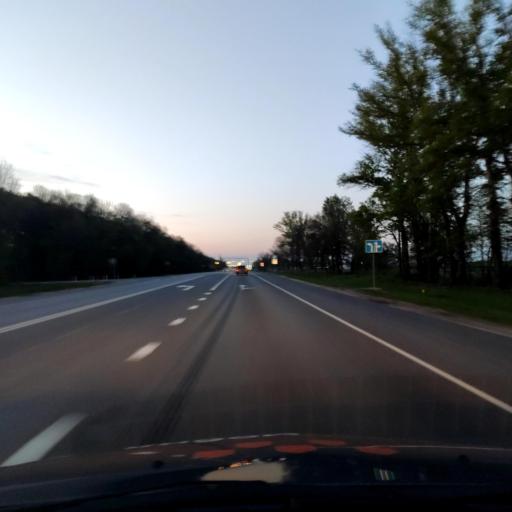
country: RU
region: Orjol
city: Zmiyevka
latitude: 52.7074
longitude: 36.3606
